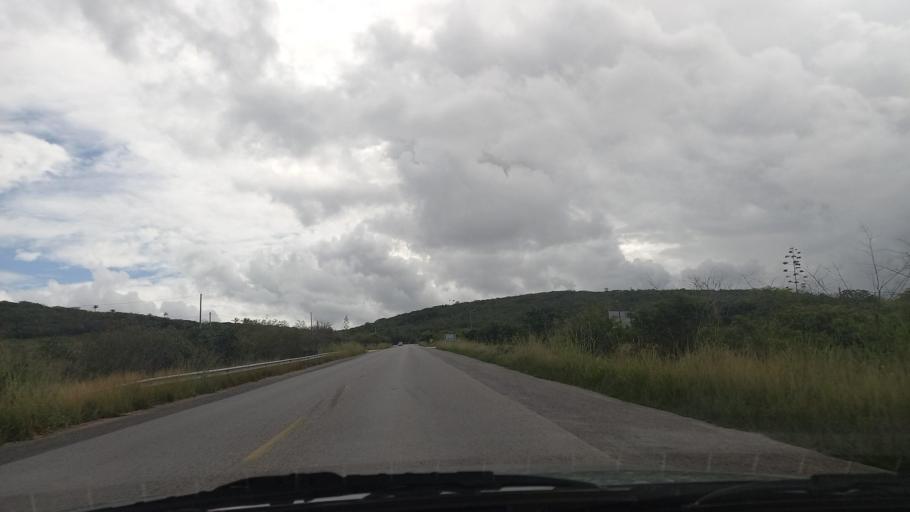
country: BR
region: Pernambuco
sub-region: Lajedo
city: Lajedo
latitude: -8.6729
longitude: -36.3949
